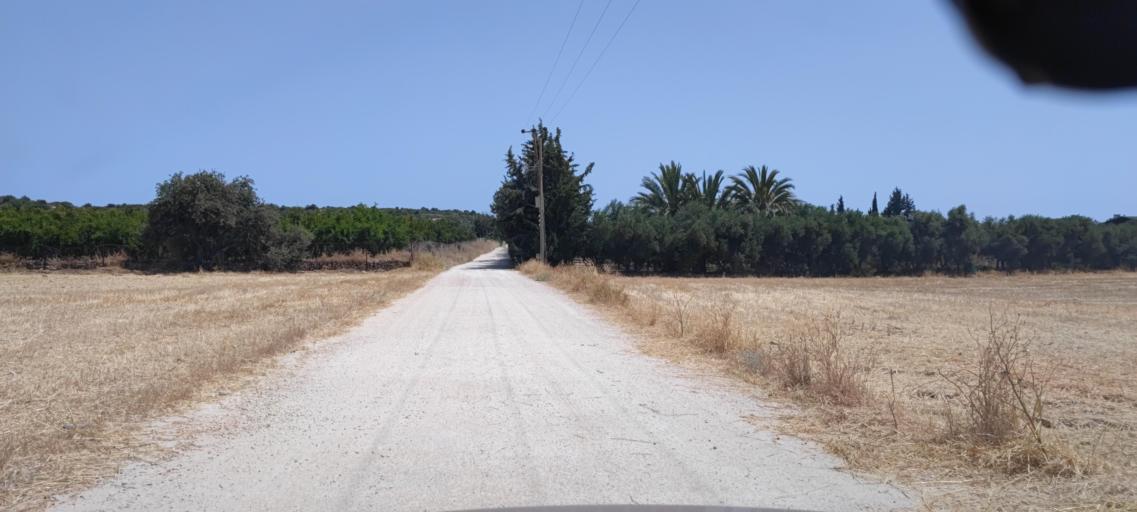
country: CY
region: Limassol
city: Pissouri
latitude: 34.7197
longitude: 32.5943
